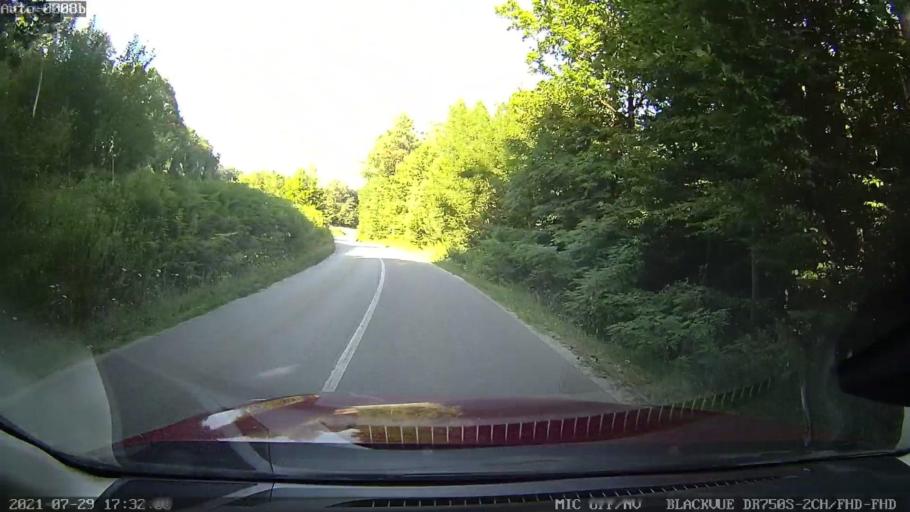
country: HR
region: Varazdinska
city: Vinica
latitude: 46.2901
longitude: 16.1279
